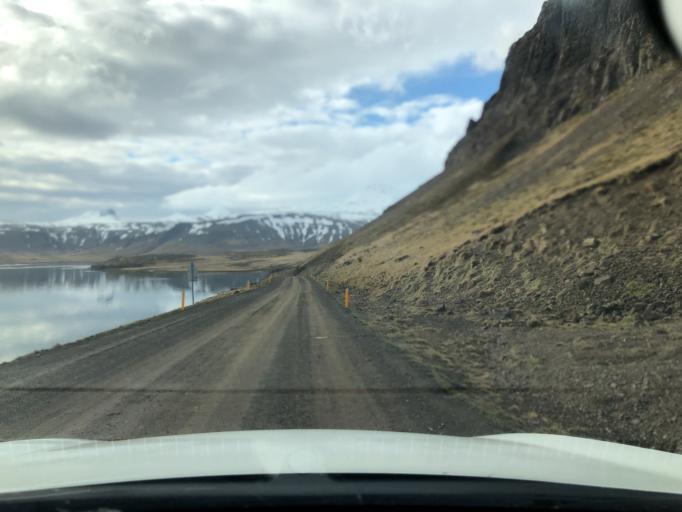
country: IS
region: West
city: Stykkisholmur
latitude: 64.9873
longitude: -22.6154
